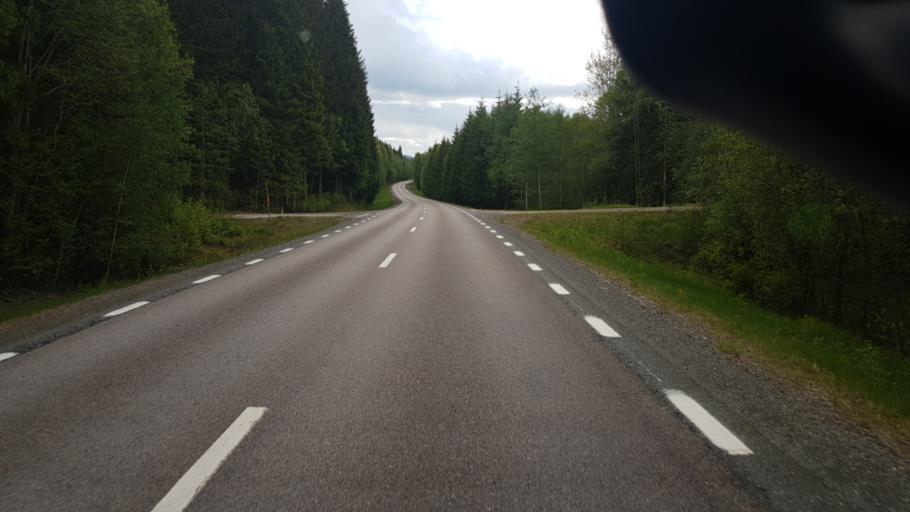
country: SE
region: Vaermland
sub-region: Arjangs Kommun
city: Arjaeng
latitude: 59.6258
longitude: 12.1408
